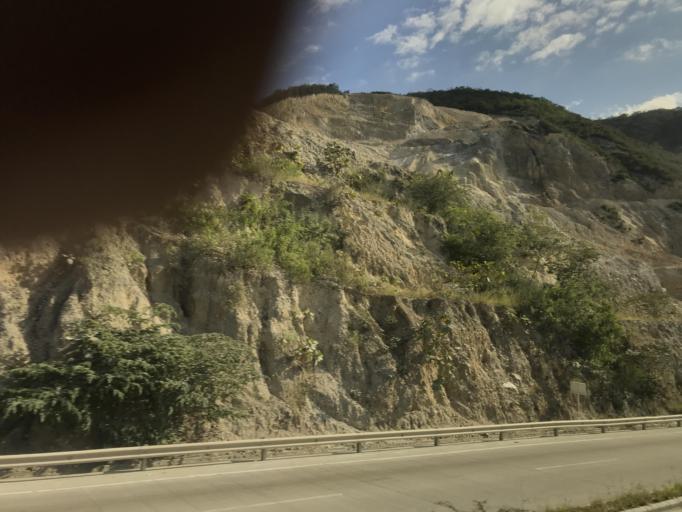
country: GT
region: El Progreso
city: Guastatoya
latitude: 14.8480
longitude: -90.1153
